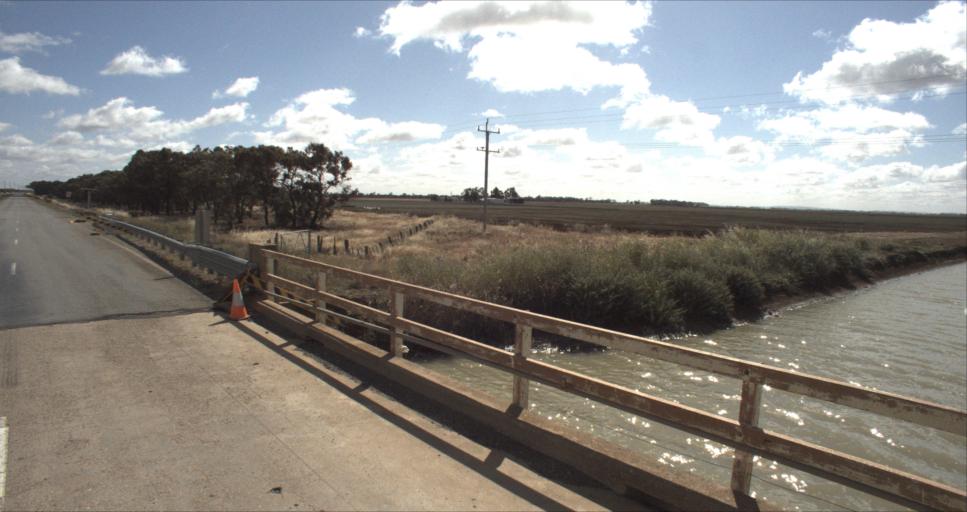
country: AU
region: New South Wales
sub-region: Murrumbidgee Shire
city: Darlington Point
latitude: -34.5528
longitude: 146.1704
